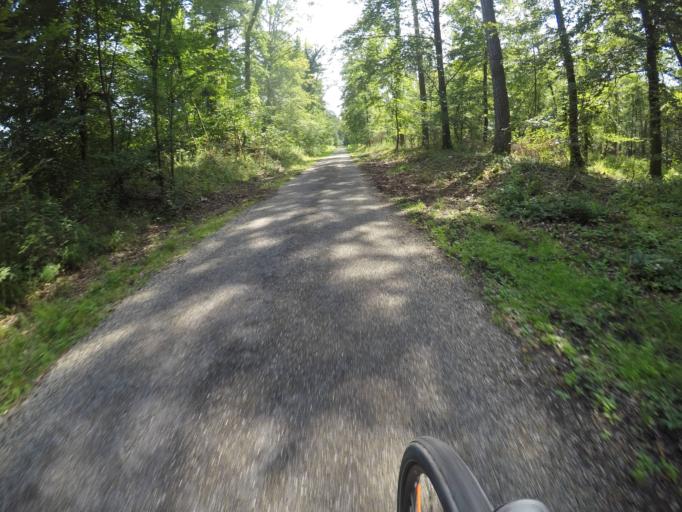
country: DE
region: Baden-Wuerttemberg
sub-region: Karlsruhe Region
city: Kronau
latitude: 49.2118
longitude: 8.5927
